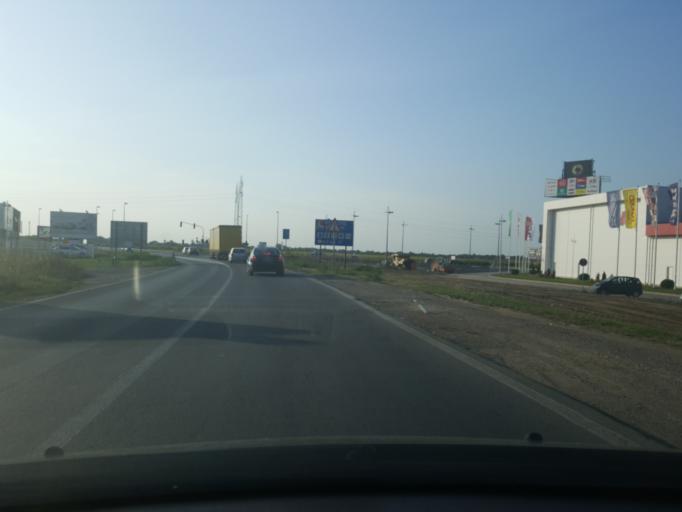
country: RS
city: Majur
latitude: 44.7529
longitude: 19.6626
